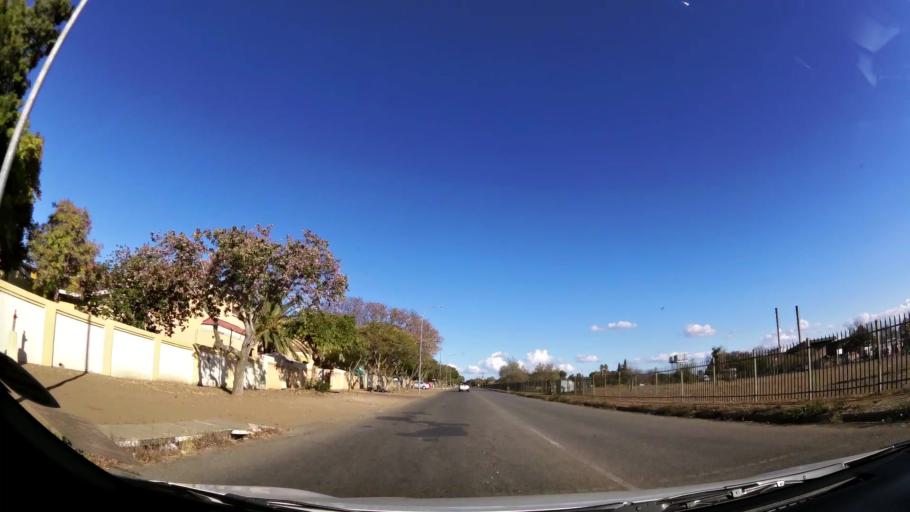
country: ZA
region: Limpopo
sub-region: Capricorn District Municipality
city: Polokwane
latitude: -23.8934
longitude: 29.4633
